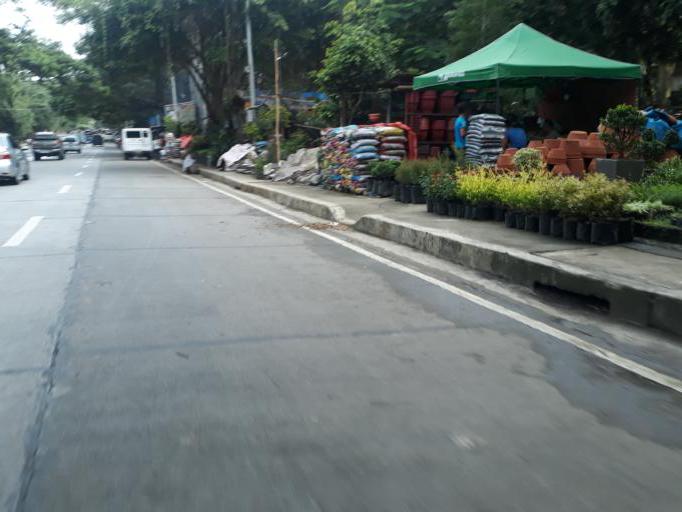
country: PH
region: Metro Manila
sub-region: Quezon City
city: Quezon City
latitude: 14.6507
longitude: 121.0593
